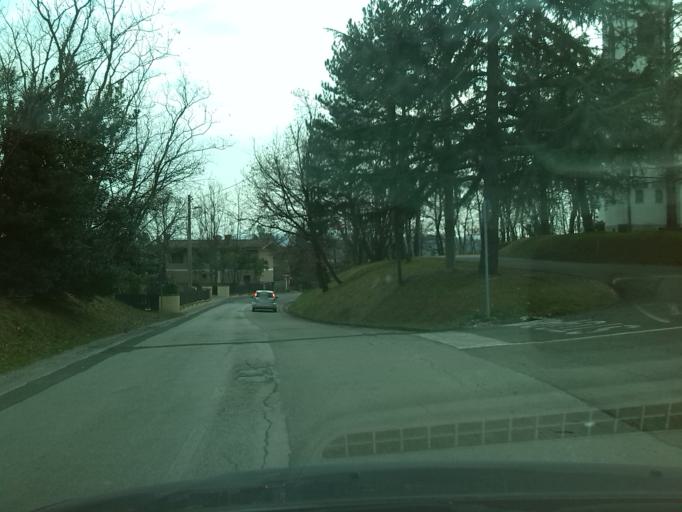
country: IT
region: Friuli Venezia Giulia
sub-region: Provincia di Gorizia
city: Mossa
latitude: 45.9655
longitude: 13.5552
